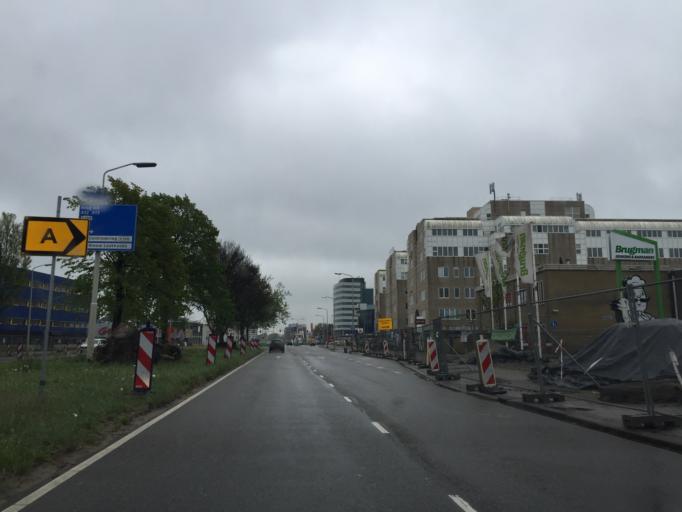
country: NL
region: South Holland
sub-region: Gemeente Leidschendam-Voorburg
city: Voorburg
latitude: 52.0712
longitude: 4.3349
